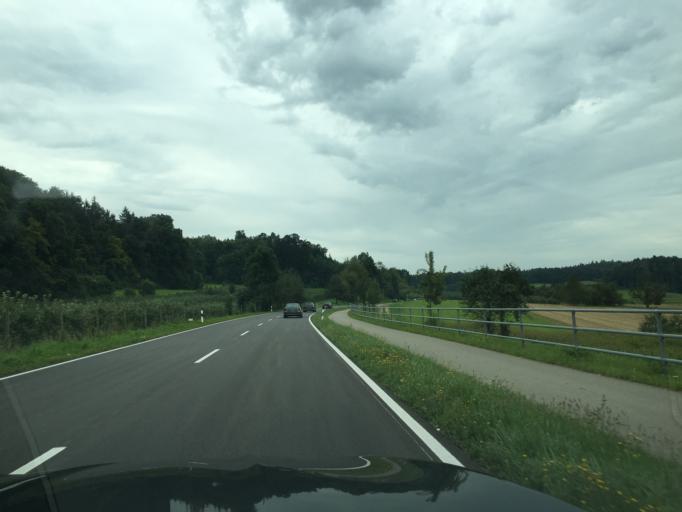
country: DE
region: Baden-Wuerttemberg
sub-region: Freiburg Region
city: Radolfzell am Bodensee
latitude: 47.7863
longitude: 8.9801
